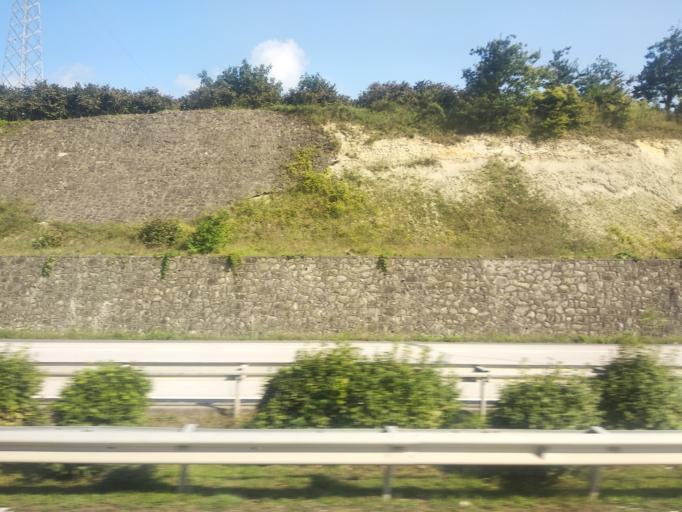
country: TR
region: Ordu
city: Ordu
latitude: 41.0036
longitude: 37.8257
